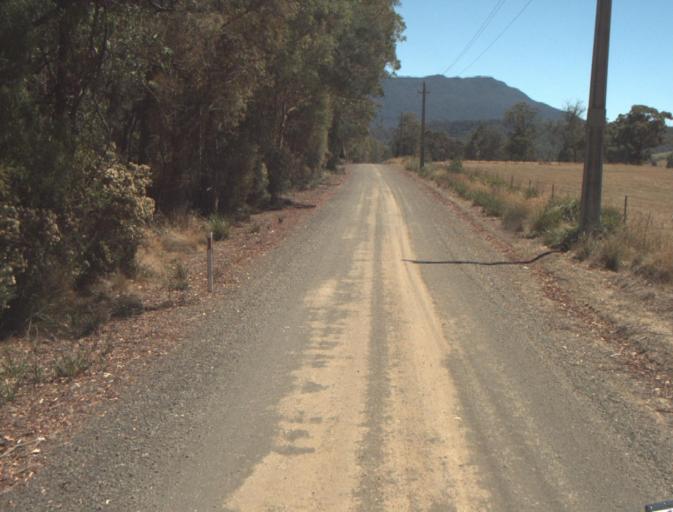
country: AU
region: Tasmania
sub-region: Launceston
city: Newstead
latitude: -41.3470
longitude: 147.3737
